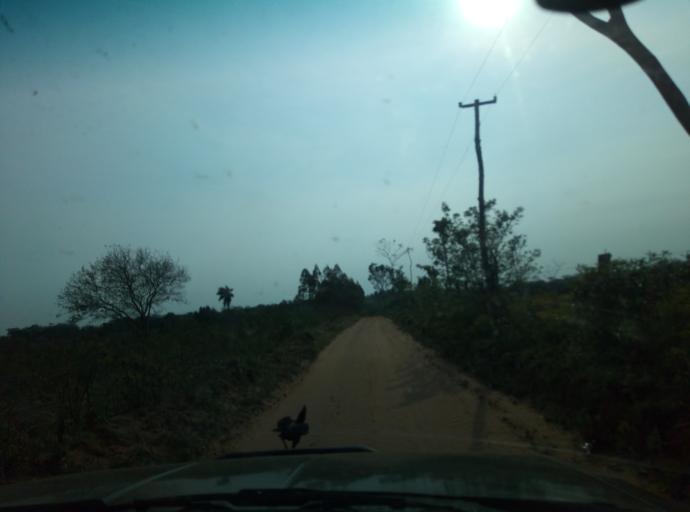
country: PY
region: Caaguazu
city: San Joaquin
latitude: -25.1550
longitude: -56.1061
